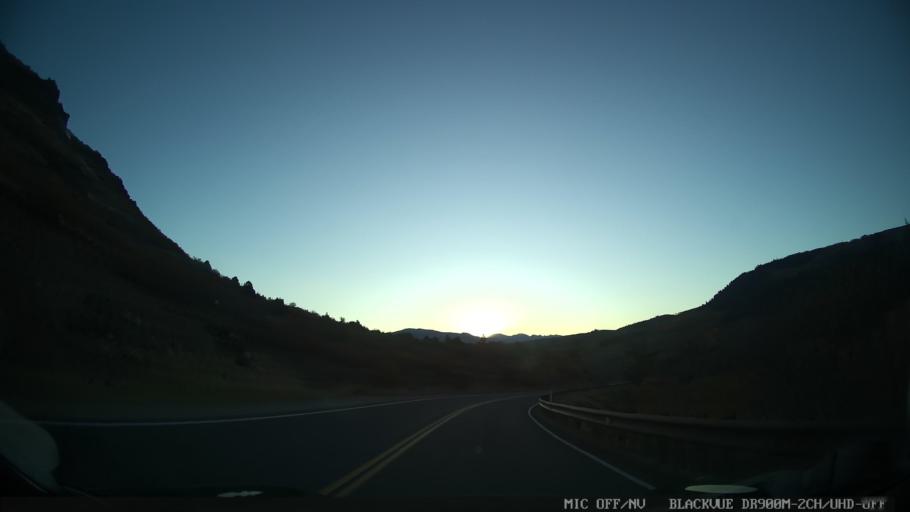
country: US
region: Colorado
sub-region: Eagle County
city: Edwards
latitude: 39.8155
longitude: -106.6688
